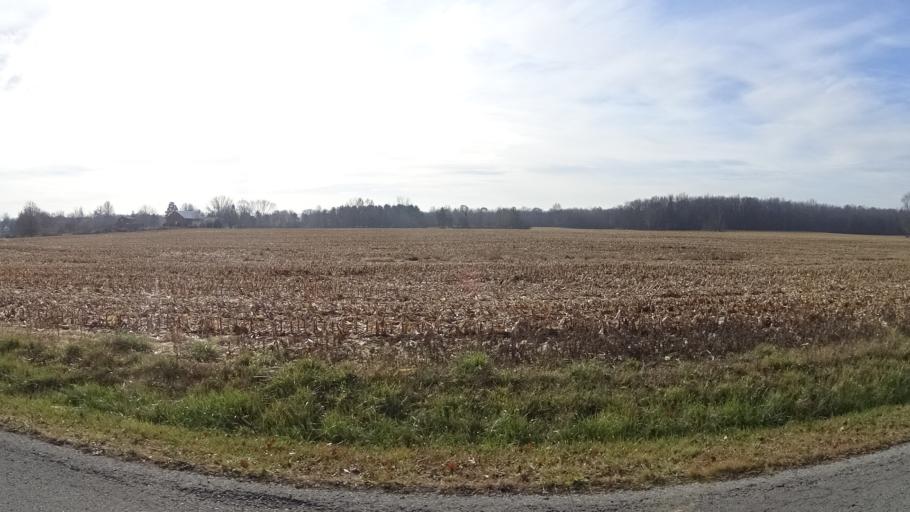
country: US
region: Ohio
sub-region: Lorain County
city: Grafton
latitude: 41.1999
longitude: -82.0559
